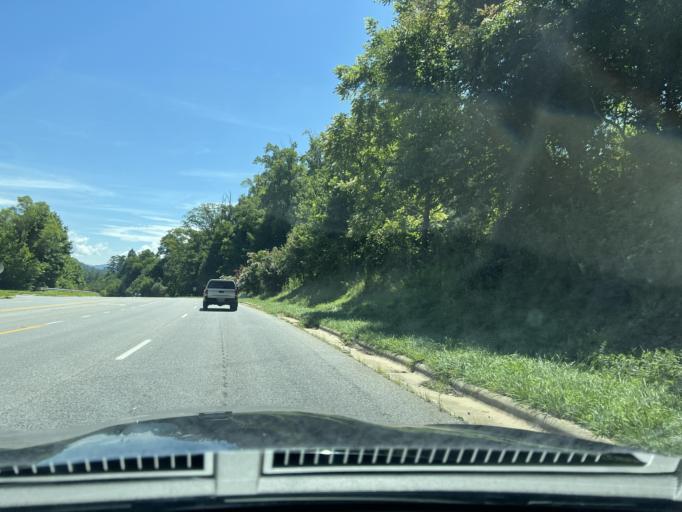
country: US
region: North Carolina
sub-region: Buncombe County
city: Fairview
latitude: 35.5460
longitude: -82.4533
